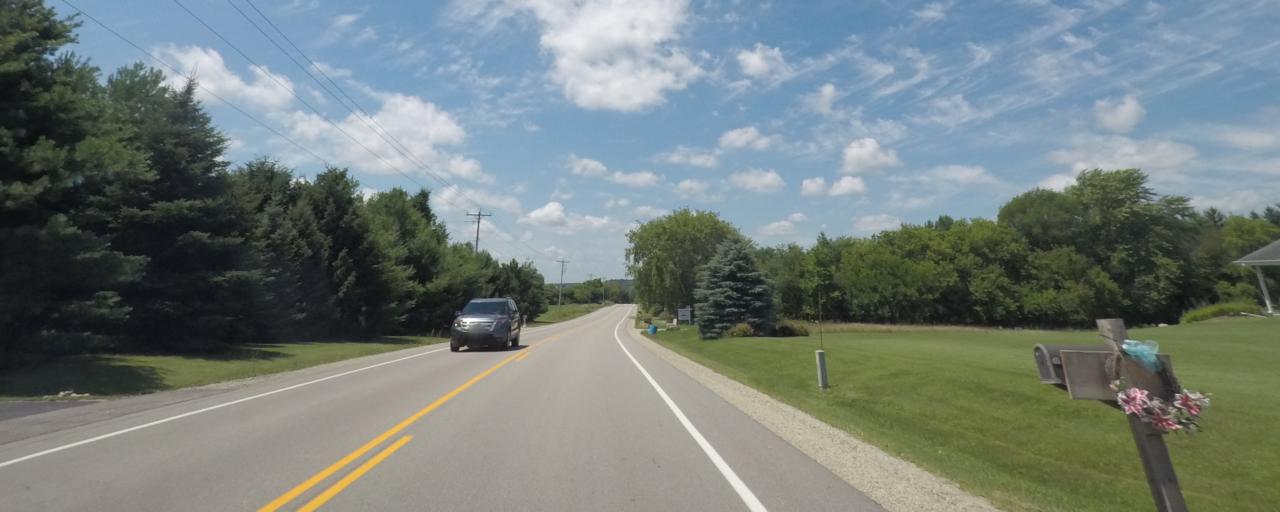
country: US
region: Wisconsin
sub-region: Jefferson County
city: Palmyra
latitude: 42.9323
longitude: -88.5758
